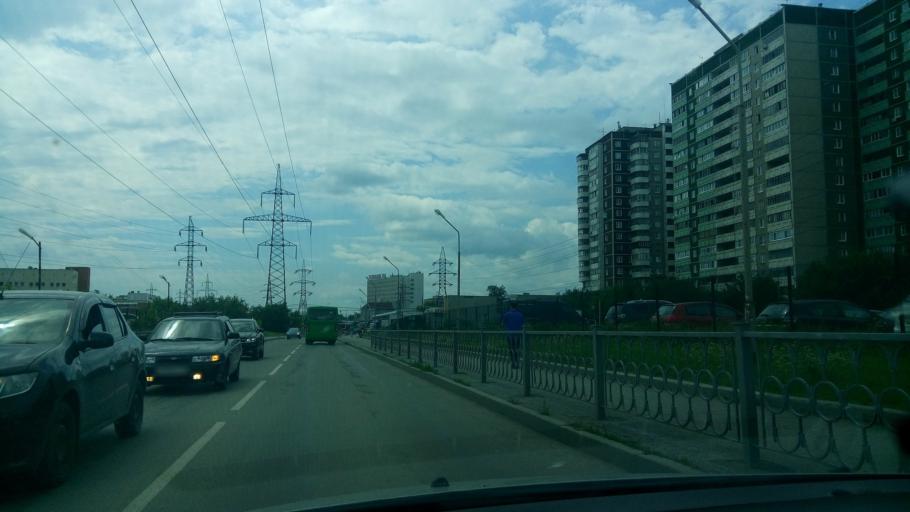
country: RU
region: Sverdlovsk
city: Yekaterinburg
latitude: 56.8650
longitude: 60.5426
